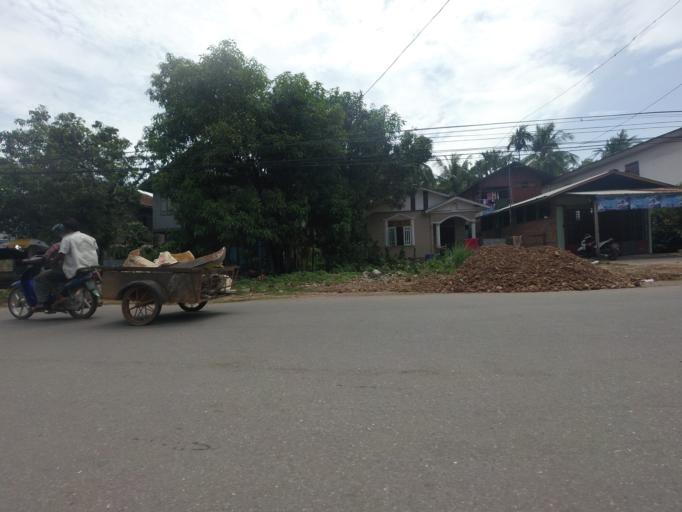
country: MM
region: Mon
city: Mawlamyine
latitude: 16.4530
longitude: 97.6272
